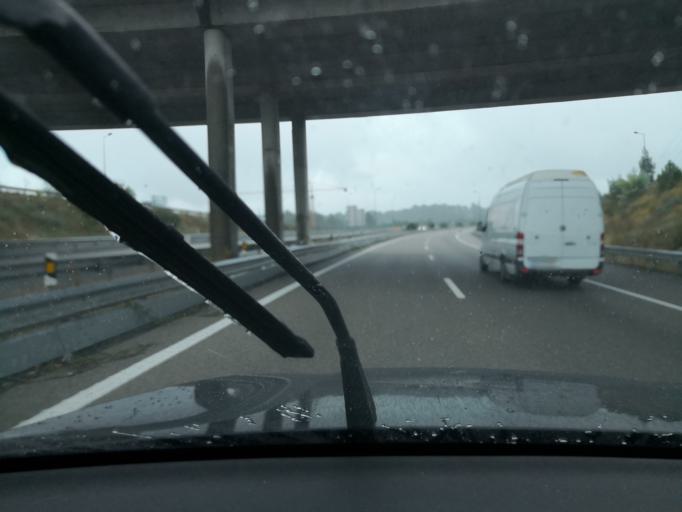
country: PT
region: Porto
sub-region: Pacos de Ferreira
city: Seroa
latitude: 41.2516
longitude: -8.4313
